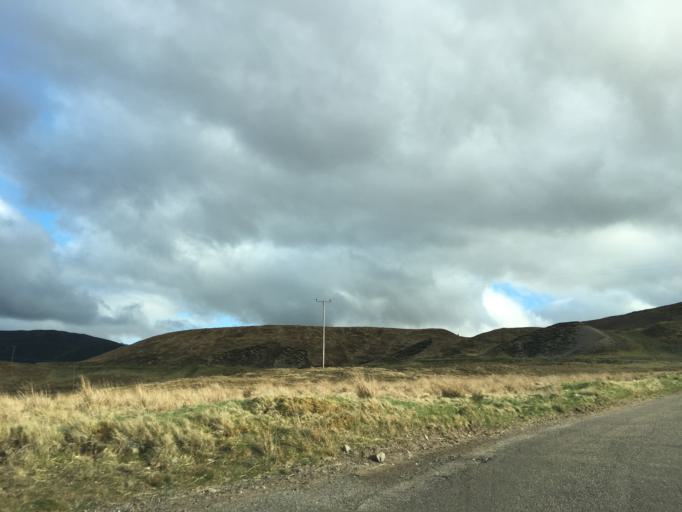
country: GB
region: Scotland
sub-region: Highland
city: Kingussie
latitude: 57.0132
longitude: -4.4188
